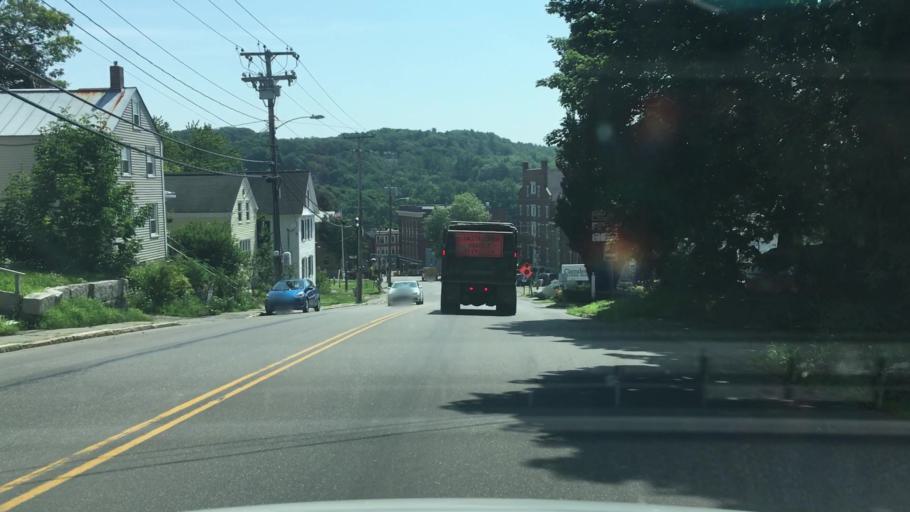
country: US
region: Maine
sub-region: Kennebec County
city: Hallowell
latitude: 44.2878
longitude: -69.7925
